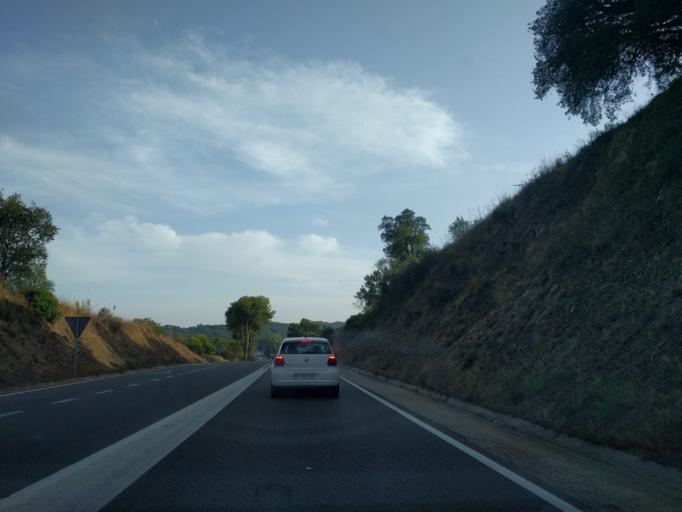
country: ES
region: Catalonia
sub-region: Provincia de Barcelona
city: Tordera
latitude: 41.6878
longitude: 2.7221
